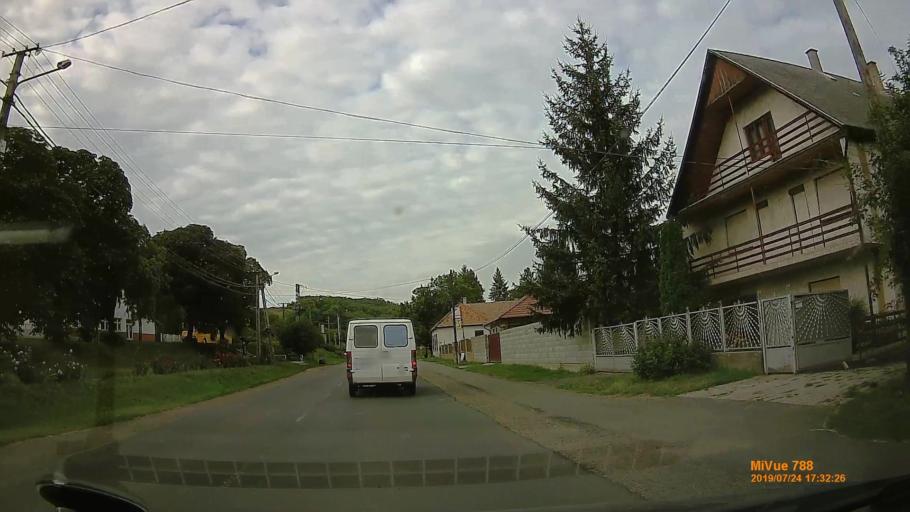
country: HU
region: Borsod-Abauj-Zemplen
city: Abaujszanto
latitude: 48.2857
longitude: 21.1816
